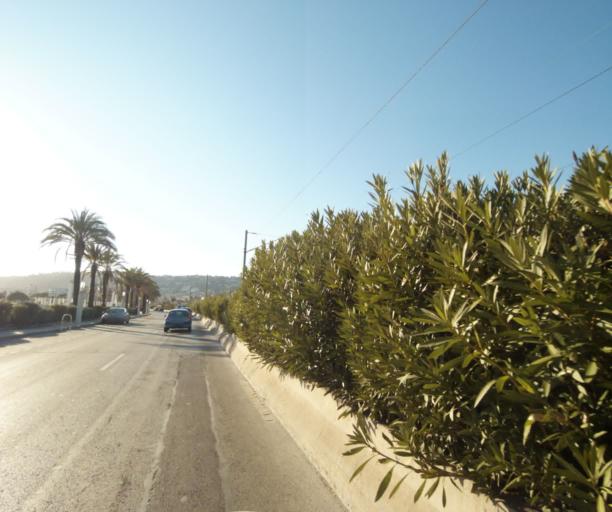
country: FR
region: Provence-Alpes-Cote d'Azur
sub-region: Departement des Alpes-Maritimes
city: Vallauris
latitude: 43.5702
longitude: 7.0871
